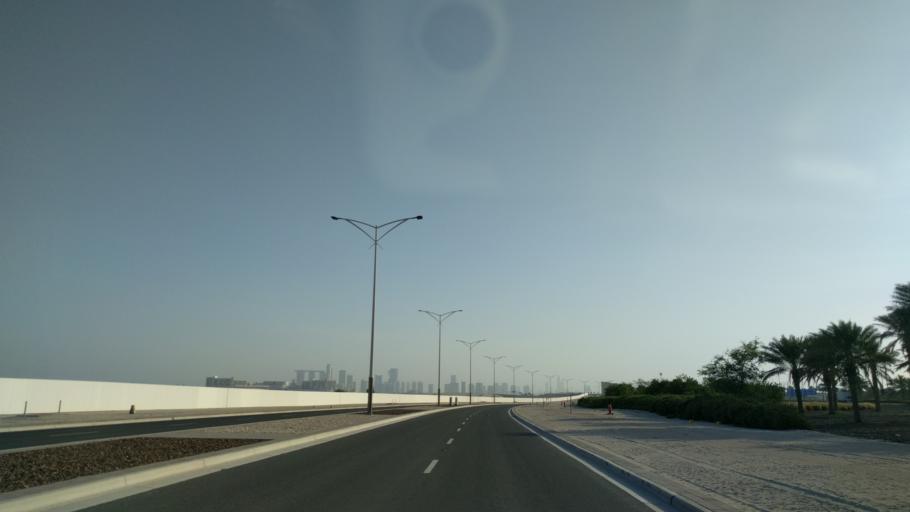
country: AE
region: Abu Dhabi
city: Abu Dhabi
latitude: 24.5445
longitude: 54.4492
